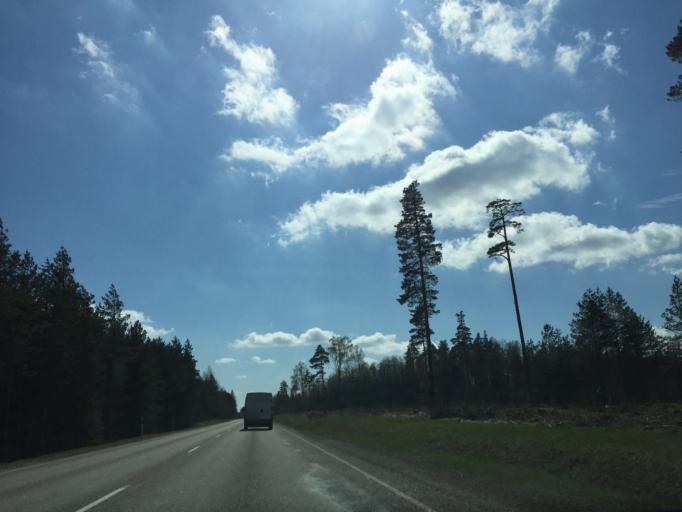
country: EE
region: Tartu
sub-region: Elva linn
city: Elva
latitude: 58.0642
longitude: 26.2004
